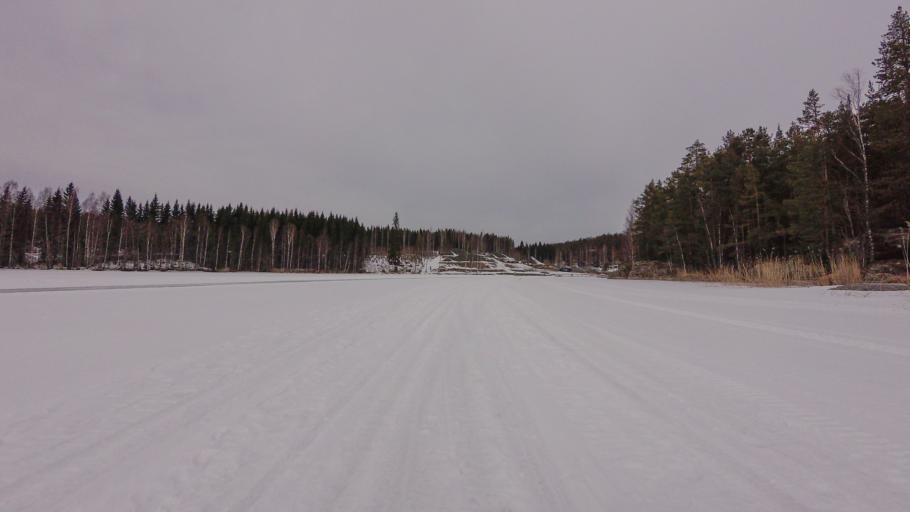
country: FI
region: Southern Savonia
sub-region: Savonlinna
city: Rantasalmi
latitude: 62.1177
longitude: 28.3138
